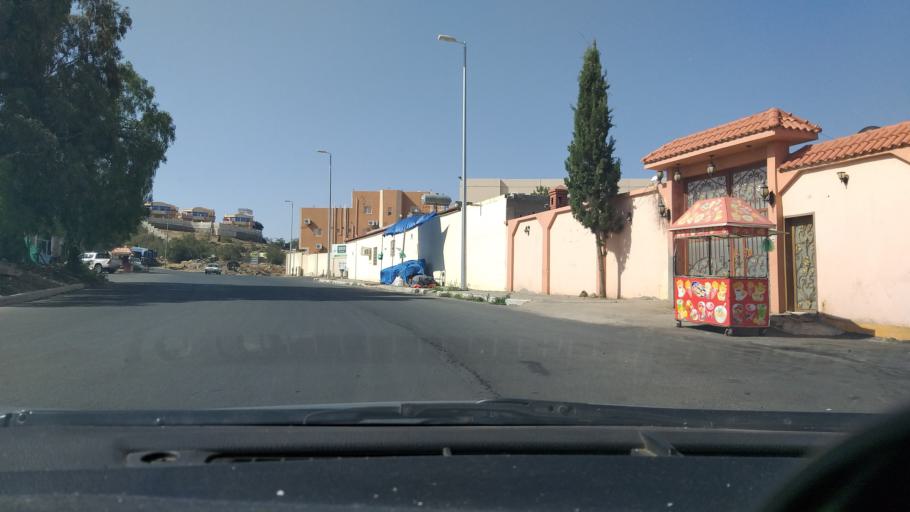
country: SA
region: Makkah
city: Ash Shafa
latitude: 21.0660
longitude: 40.3212
